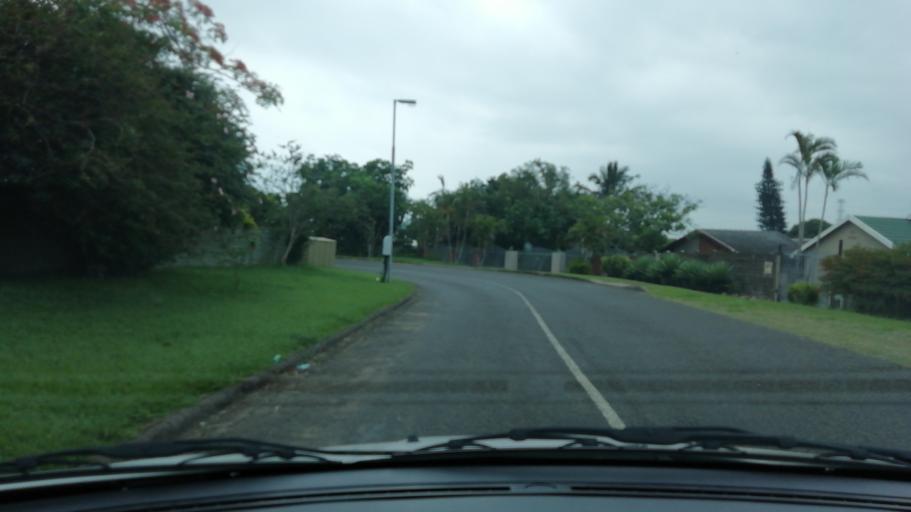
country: ZA
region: KwaZulu-Natal
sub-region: uThungulu District Municipality
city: Empangeni
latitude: -28.7347
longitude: 31.9000
